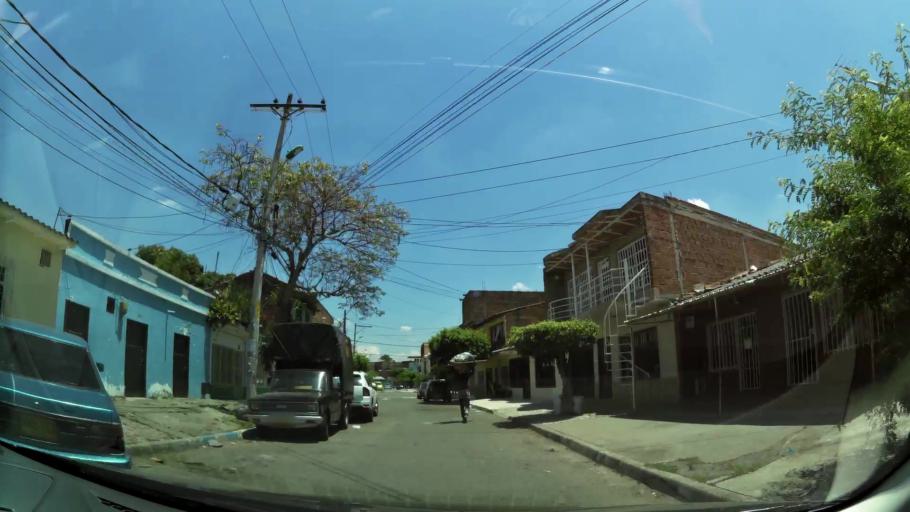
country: CO
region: Valle del Cauca
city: Cali
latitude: 3.4298
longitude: -76.5056
